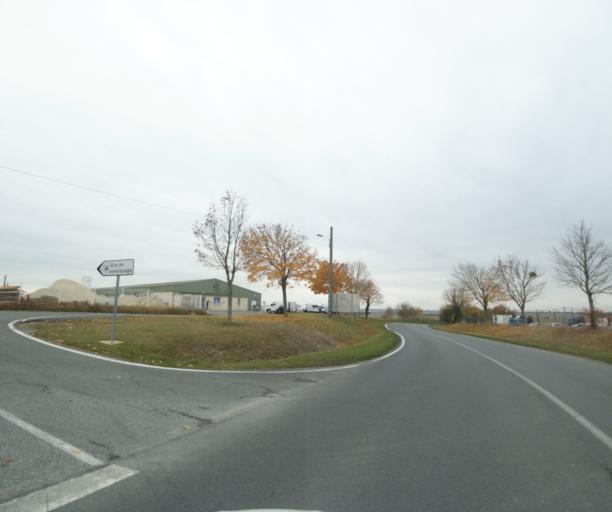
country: FR
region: Poitou-Charentes
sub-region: Departement de la Charente-Maritime
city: Les Gonds
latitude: 45.7198
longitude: -0.6443
